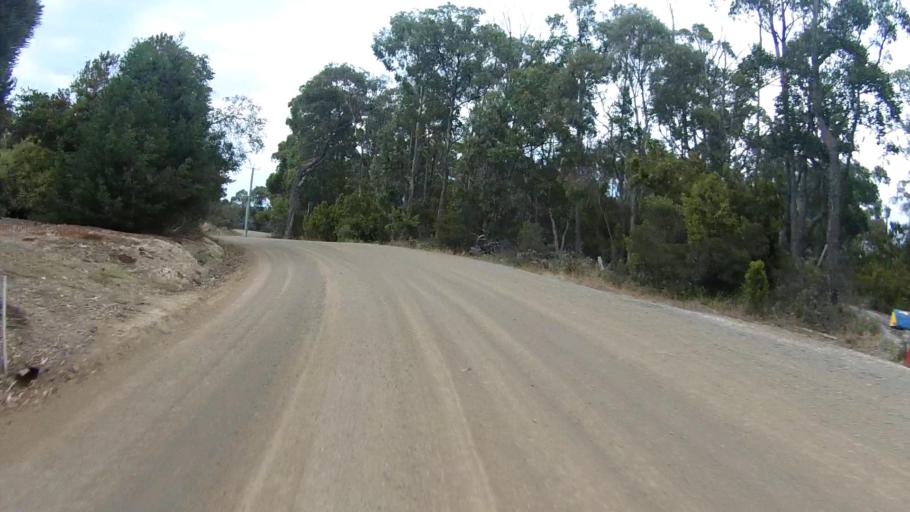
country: AU
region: Tasmania
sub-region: Huon Valley
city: Cygnet
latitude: -43.2268
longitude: 147.0962
